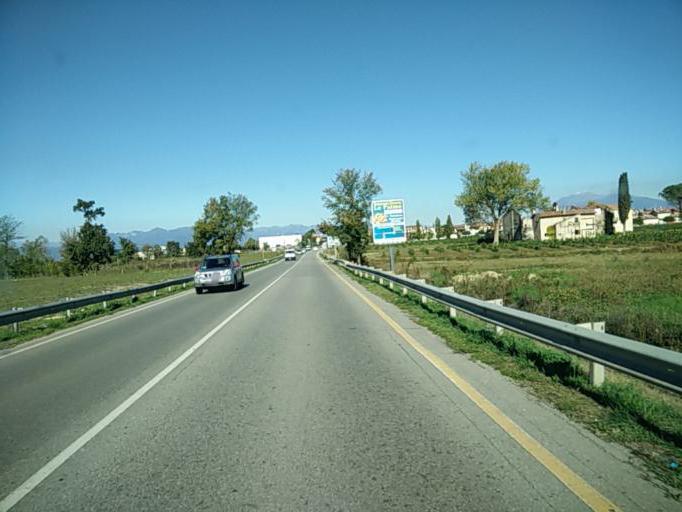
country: IT
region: Lombardy
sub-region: Provincia di Brescia
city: San Martino della Battaglia
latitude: 45.4584
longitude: 10.6001
